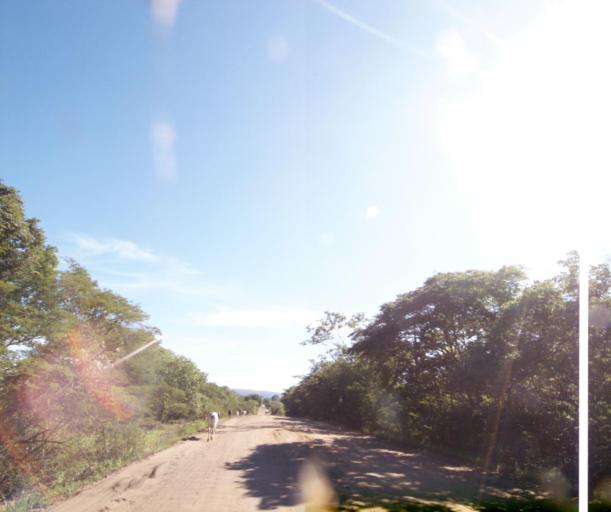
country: BR
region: Bahia
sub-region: Sao Felix Do Coribe
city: Santa Maria da Vitoria
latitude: -13.6311
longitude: -44.4274
